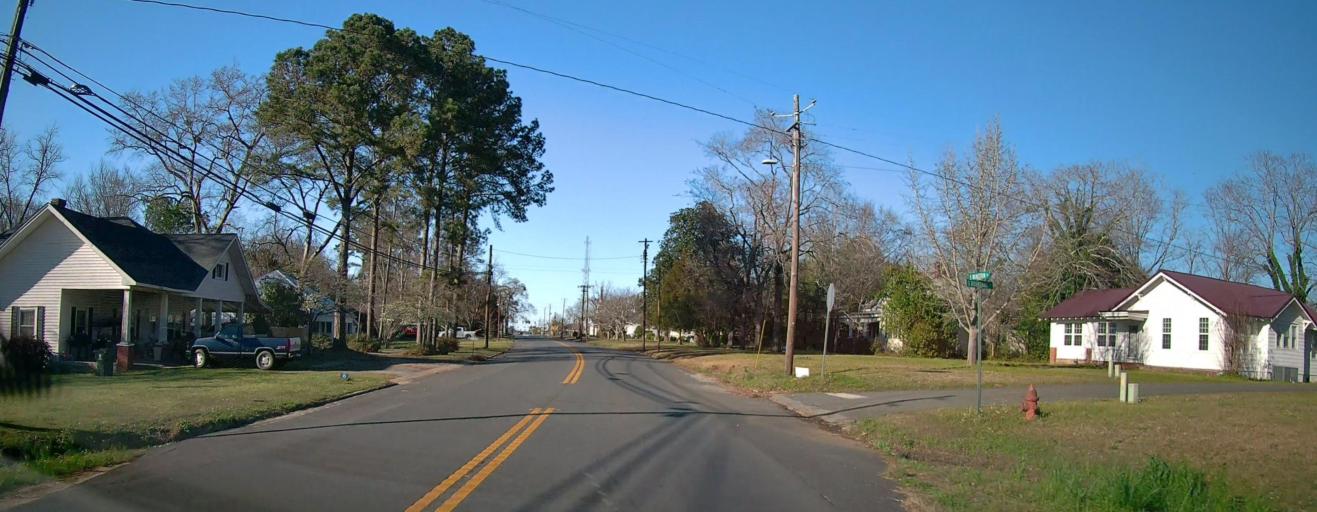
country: US
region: Georgia
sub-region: Taylor County
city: Reynolds
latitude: 32.5548
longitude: -84.0963
